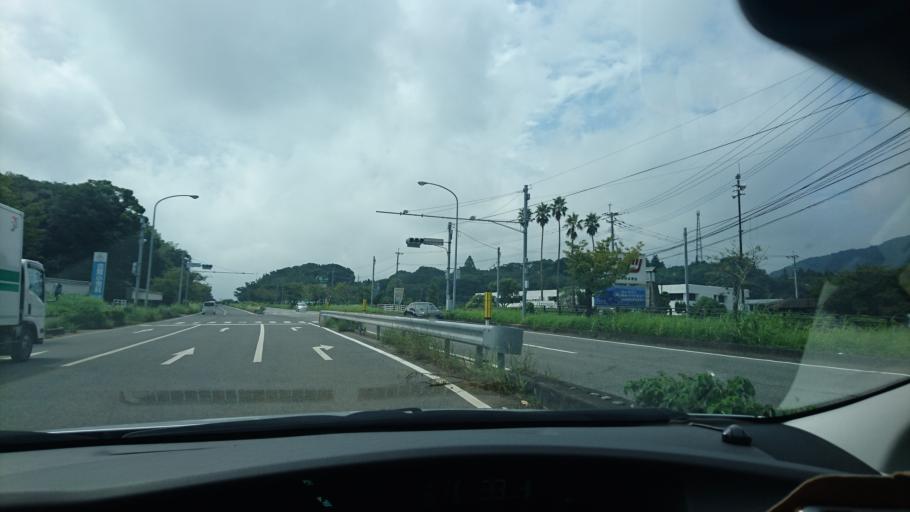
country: JP
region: Saga Prefecture
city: Saga-shi
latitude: 33.2313
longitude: 130.1806
